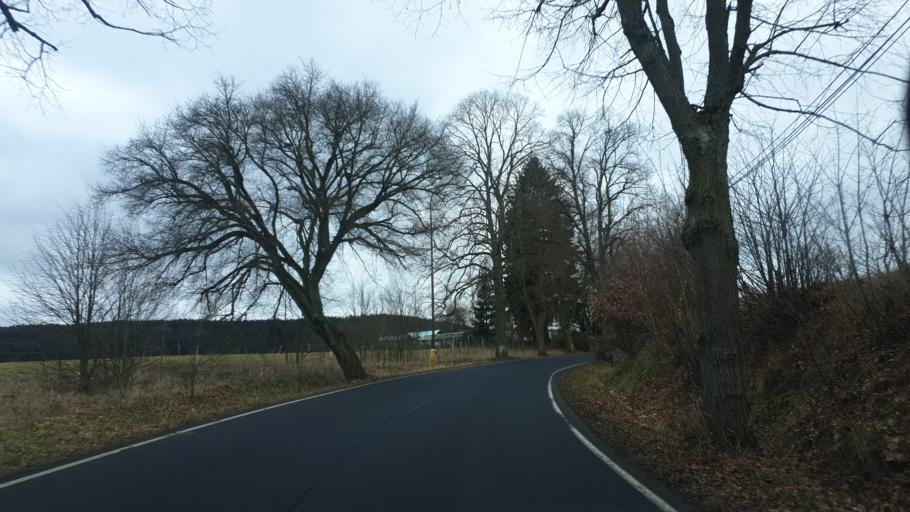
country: DE
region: Saxony
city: Bad Elster
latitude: 50.2590
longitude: 12.2259
